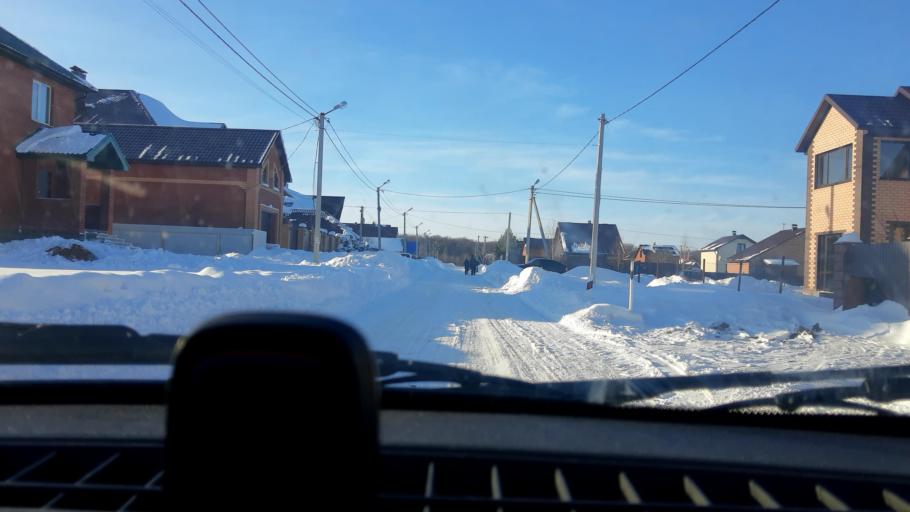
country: RU
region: Bashkortostan
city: Kabakovo
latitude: 54.6205
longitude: 56.0859
